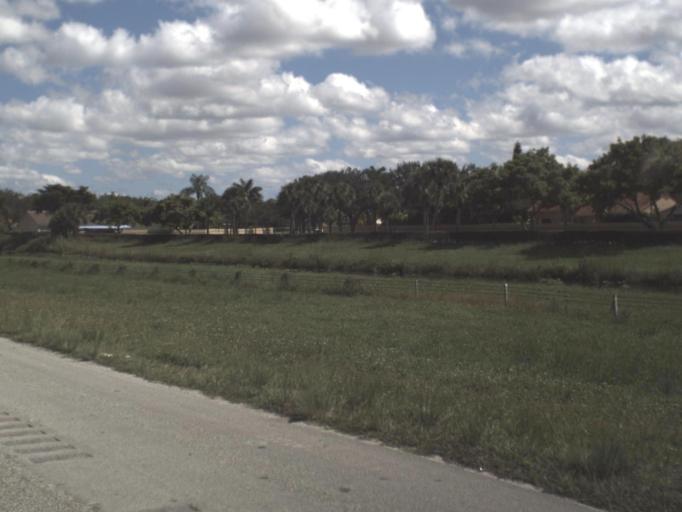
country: US
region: Florida
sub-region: Miami-Dade County
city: Palm Springs North
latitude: 25.9507
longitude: -80.3488
